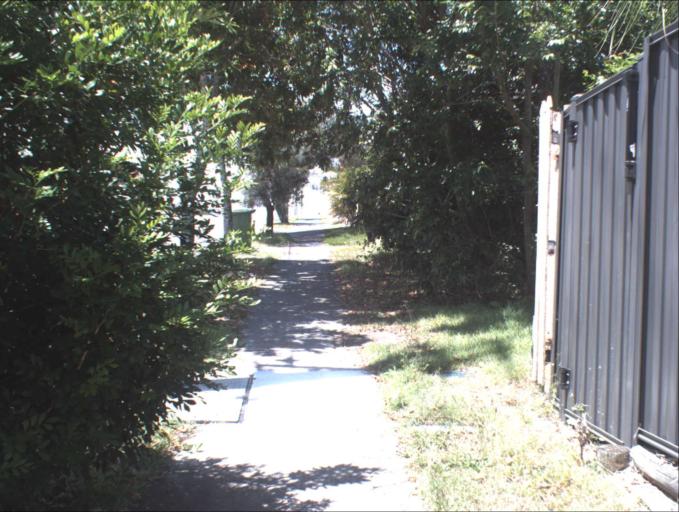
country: AU
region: Queensland
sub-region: Logan
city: Rochedale South
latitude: -27.5941
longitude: 153.1382
